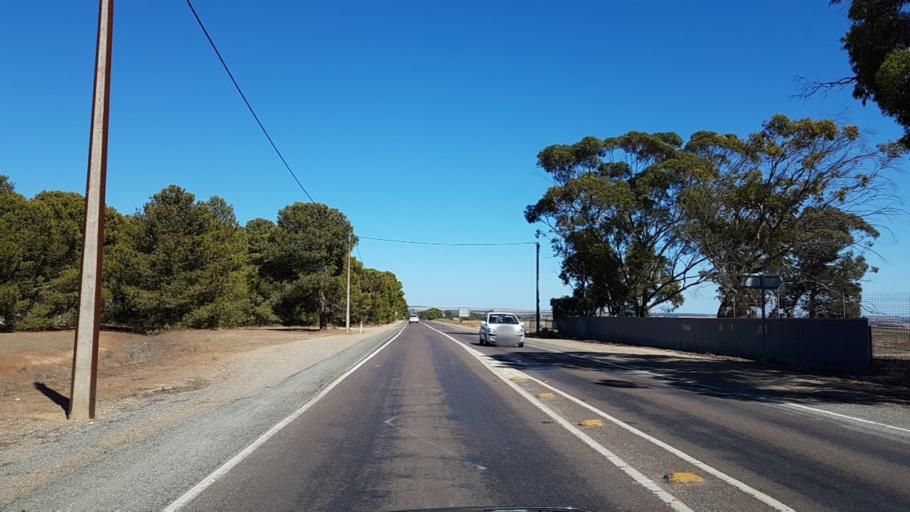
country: AU
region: South Australia
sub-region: Copper Coast
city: Kadina
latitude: -34.0594
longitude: 138.0358
